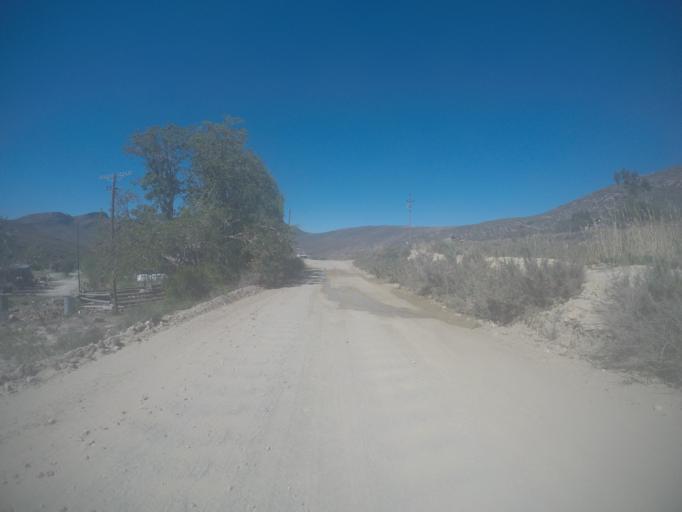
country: ZA
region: Western Cape
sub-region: West Coast District Municipality
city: Clanwilliam
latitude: -32.5506
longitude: 19.3608
